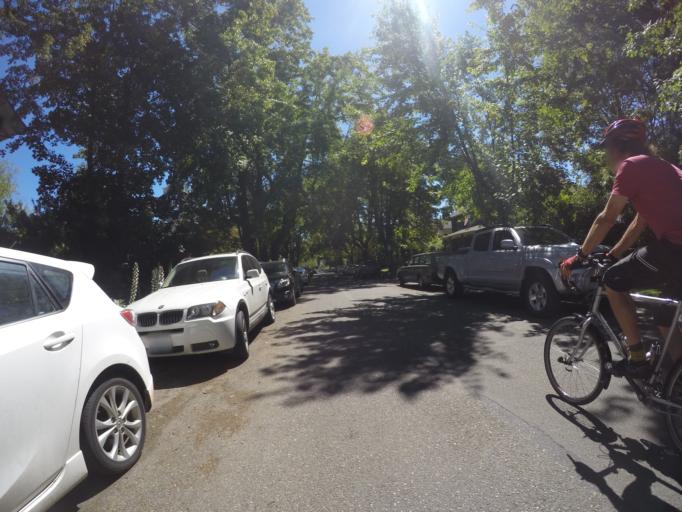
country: US
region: Washington
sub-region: King County
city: Seattle
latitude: 47.6259
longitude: -122.3146
